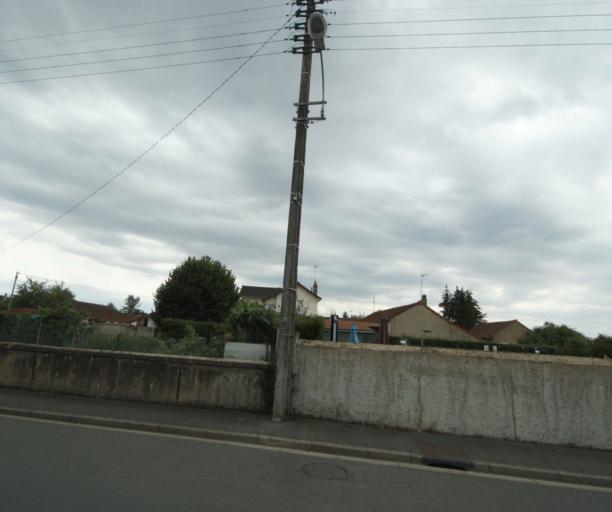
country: FR
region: Bourgogne
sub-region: Departement de Saone-et-Loire
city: Gueugnon
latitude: 46.6039
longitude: 4.0548
